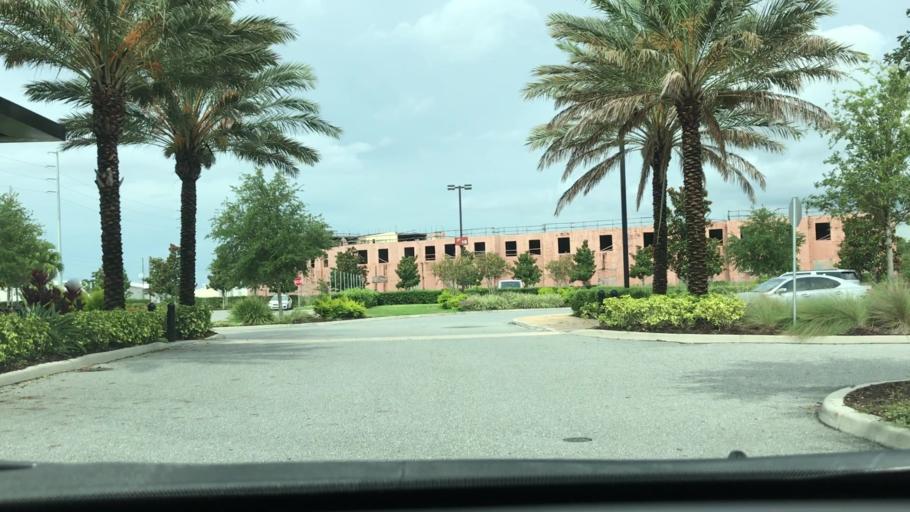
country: US
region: Florida
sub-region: Orange County
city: Williamsburg
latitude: 28.3908
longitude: -81.4899
